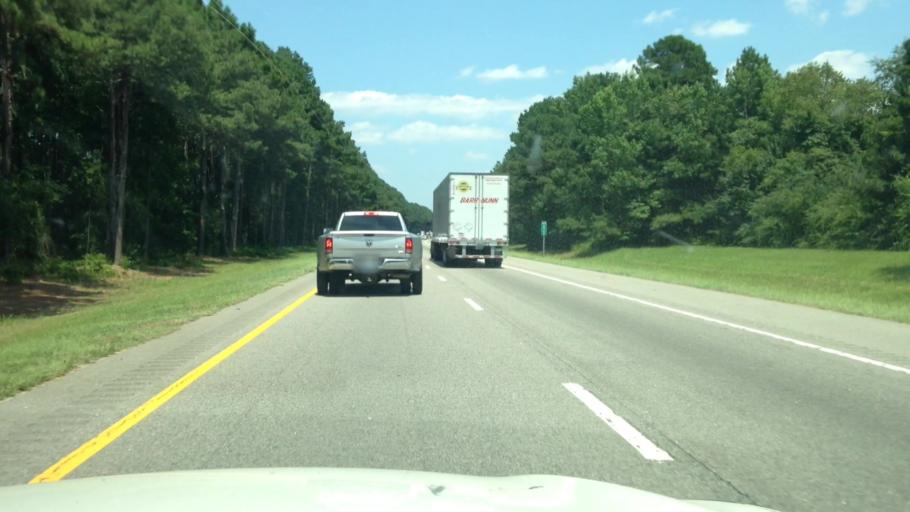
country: US
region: North Carolina
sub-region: Robeson County
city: Fairmont
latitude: 34.5809
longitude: -79.1430
